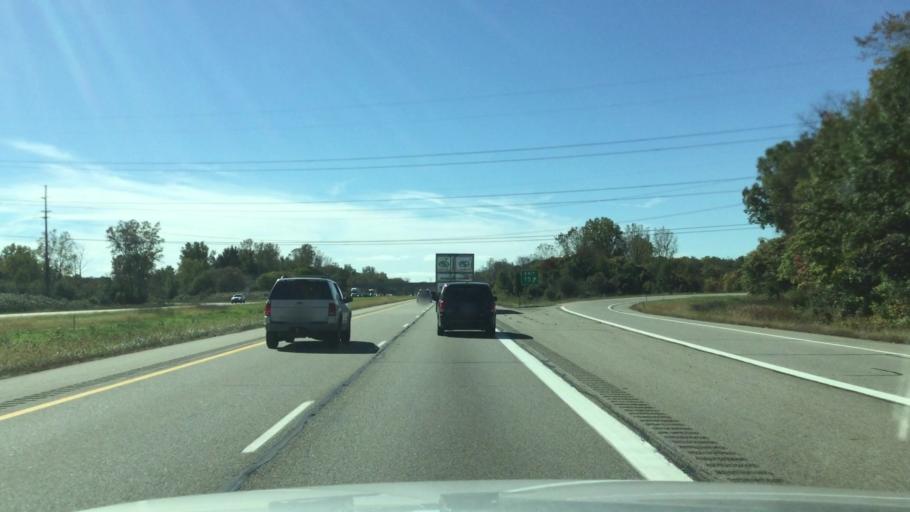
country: US
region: Michigan
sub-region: Wayne County
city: Plymouth
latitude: 42.3638
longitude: -83.5617
